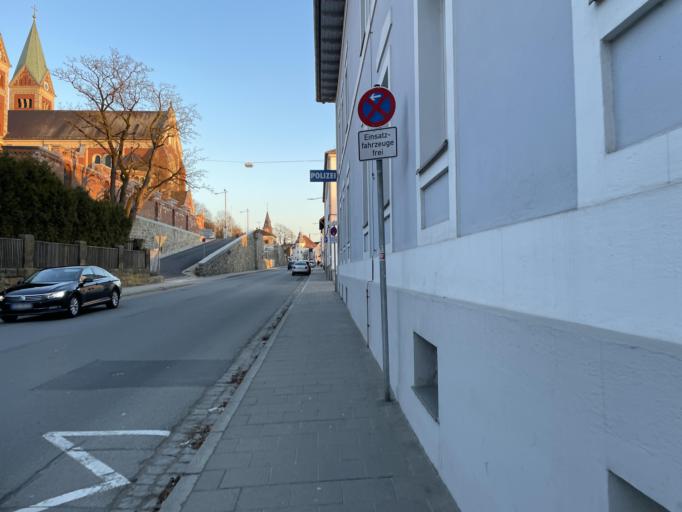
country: DE
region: Bavaria
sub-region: Upper Palatinate
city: Cham
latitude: 49.2221
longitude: 12.6605
